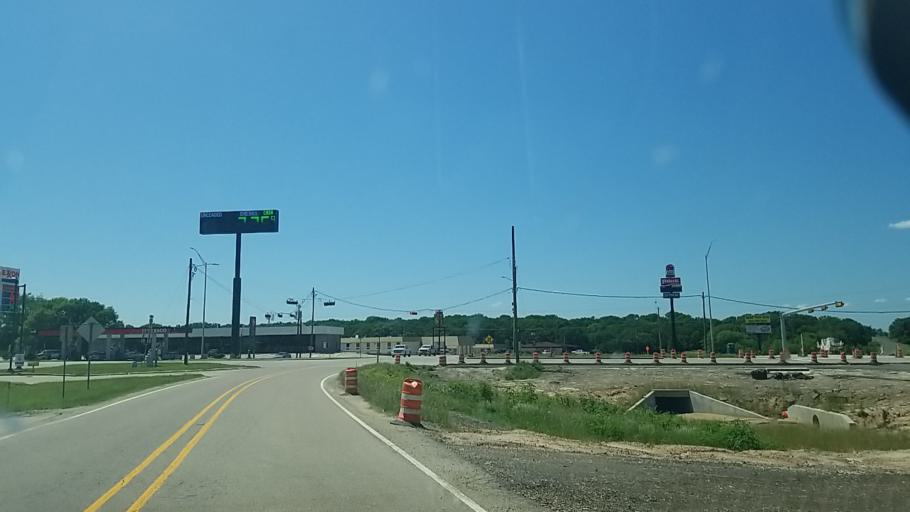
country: US
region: Texas
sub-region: Leon County
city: Buffalo
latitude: 31.4492
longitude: -96.0765
